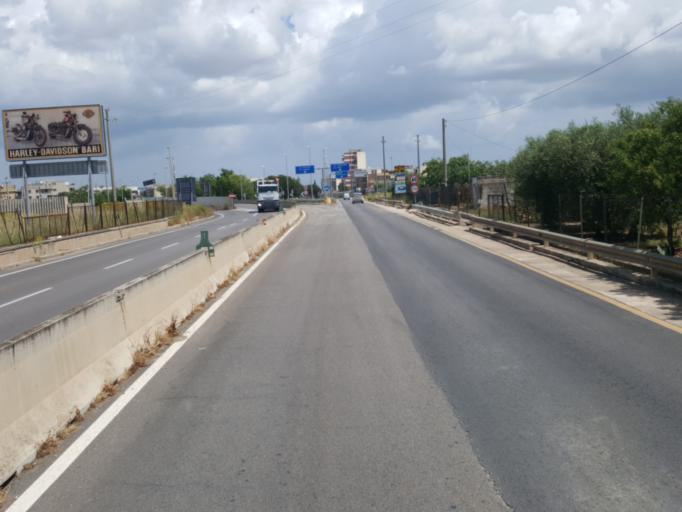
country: IT
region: Apulia
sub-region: Provincia di Bari
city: Modugno
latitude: 41.0841
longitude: 16.7712
